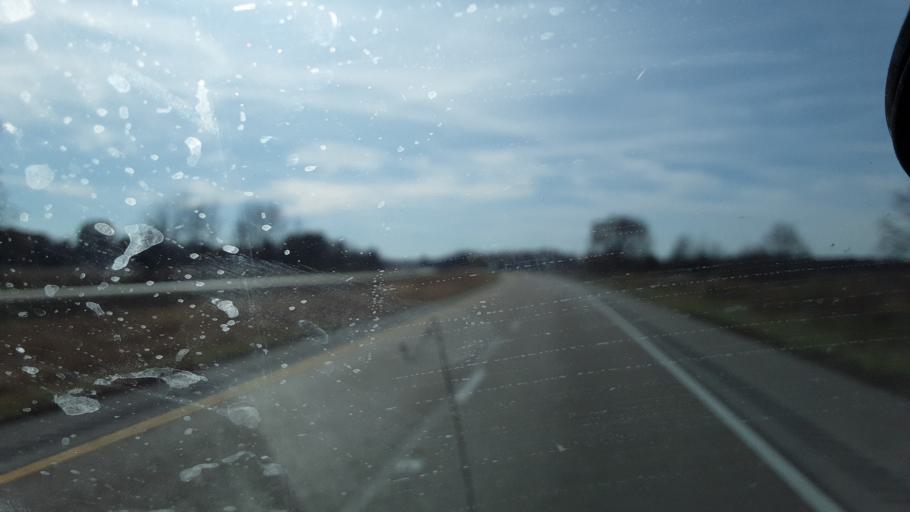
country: US
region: Illinois
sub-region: Cumberland County
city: Greenup
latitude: 39.2727
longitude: -88.1080
